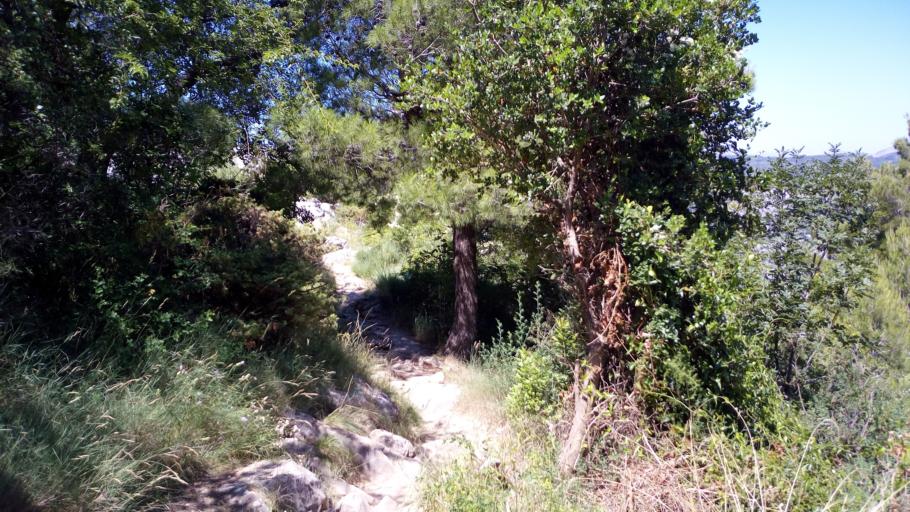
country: HR
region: Splitsko-Dalmatinska
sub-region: Grad Omis
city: Omis
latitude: 43.4444
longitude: 16.7024
